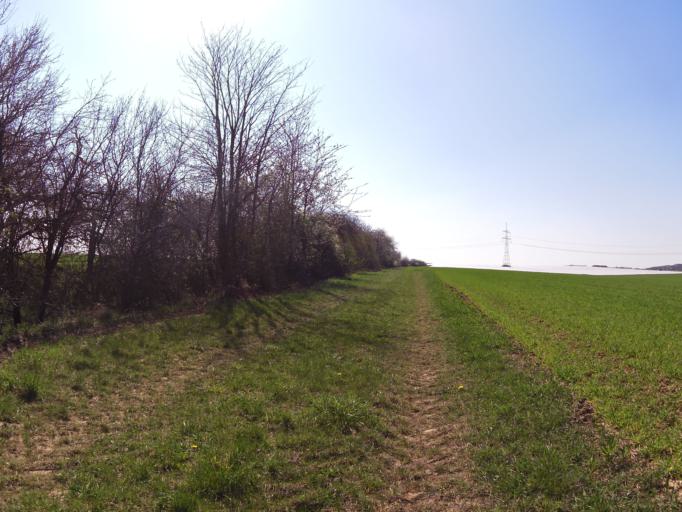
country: DE
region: Bavaria
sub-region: Regierungsbezirk Unterfranken
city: Oberpleichfeld
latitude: 49.8224
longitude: 10.0951
